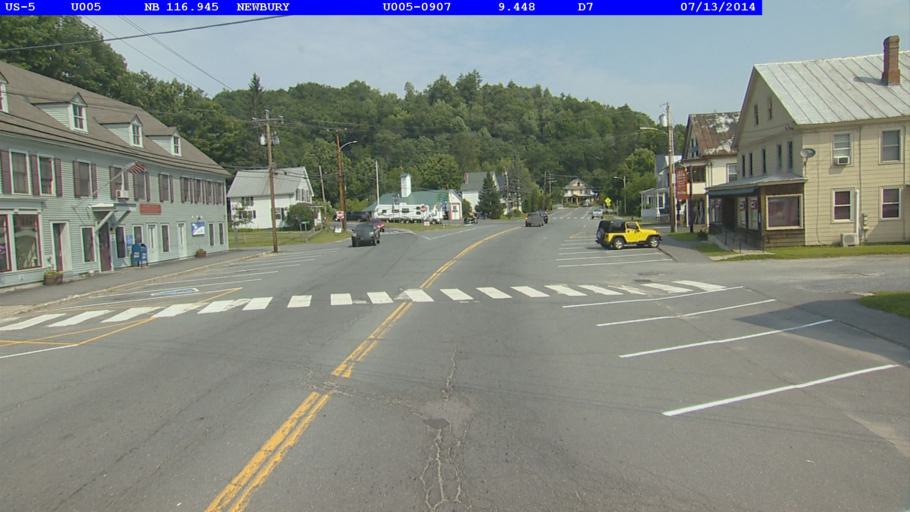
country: US
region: New Hampshire
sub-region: Grafton County
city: Woodsville
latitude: 44.1534
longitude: -72.0468
